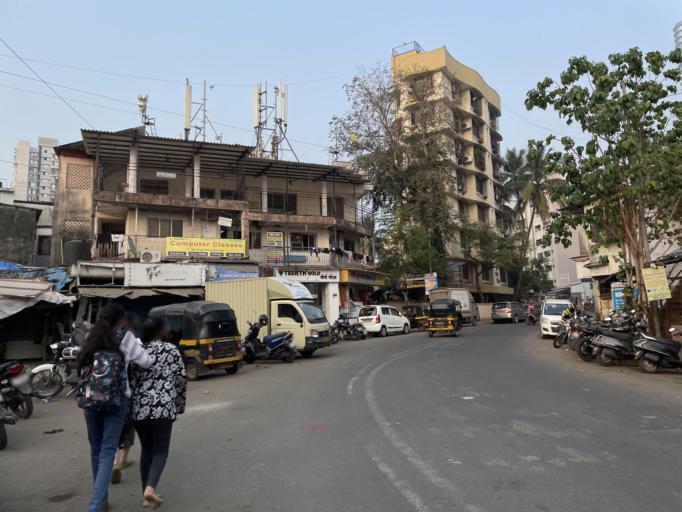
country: IN
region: Maharashtra
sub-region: Mumbai Suburban
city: Borivli
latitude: 19.2384
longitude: 72.8452
